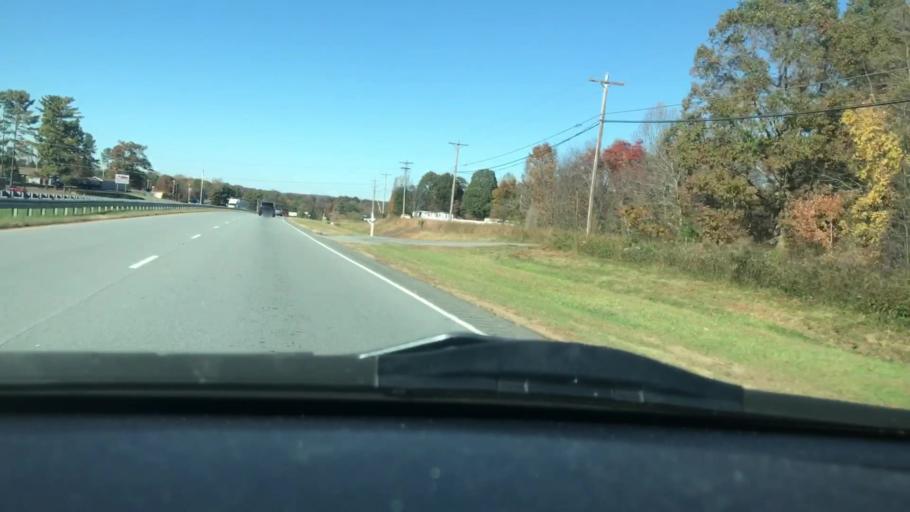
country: US
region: North Carolina
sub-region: Rockingham County
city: Madison
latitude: 36.3510
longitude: -79.9455
